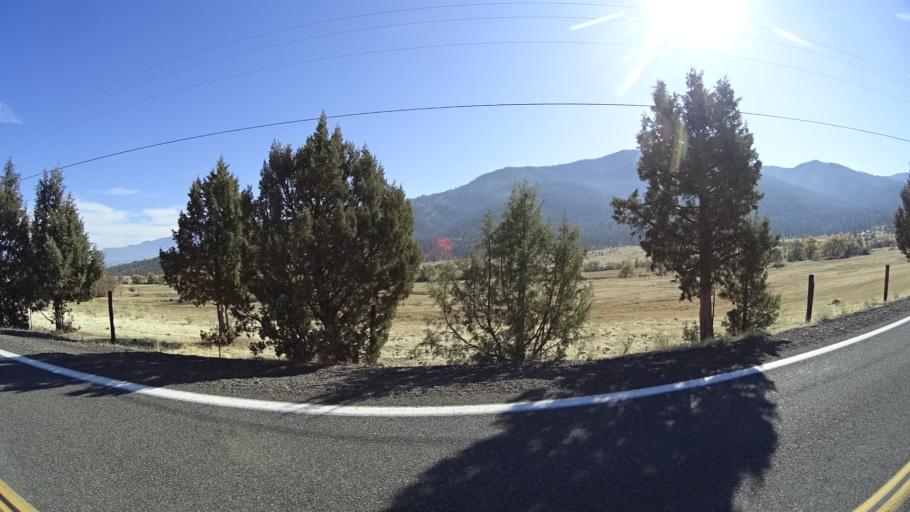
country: US
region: California
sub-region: Siskiyou County
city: Weed
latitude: 41.4920
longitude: -122.5574
